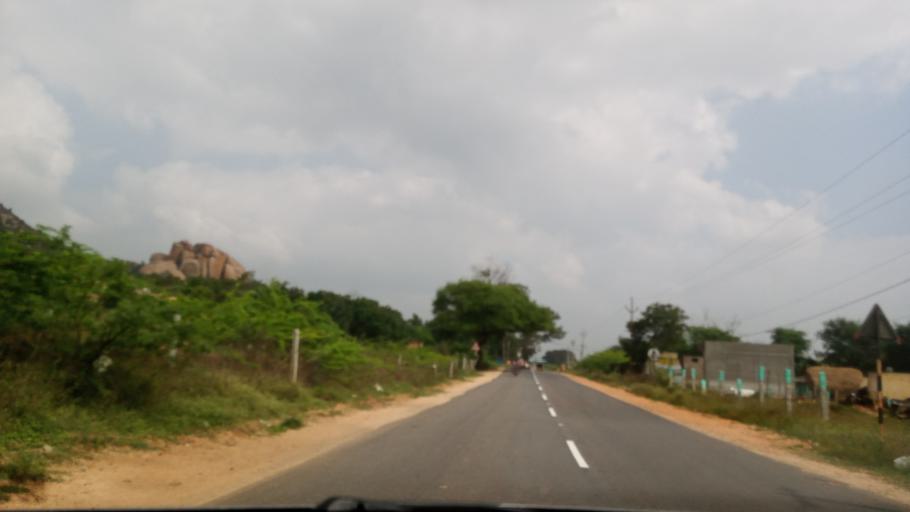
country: IN
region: Andhra Pradesh
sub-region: Chittoor
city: Madanapalle
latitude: 13.6341
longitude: 78.6174
